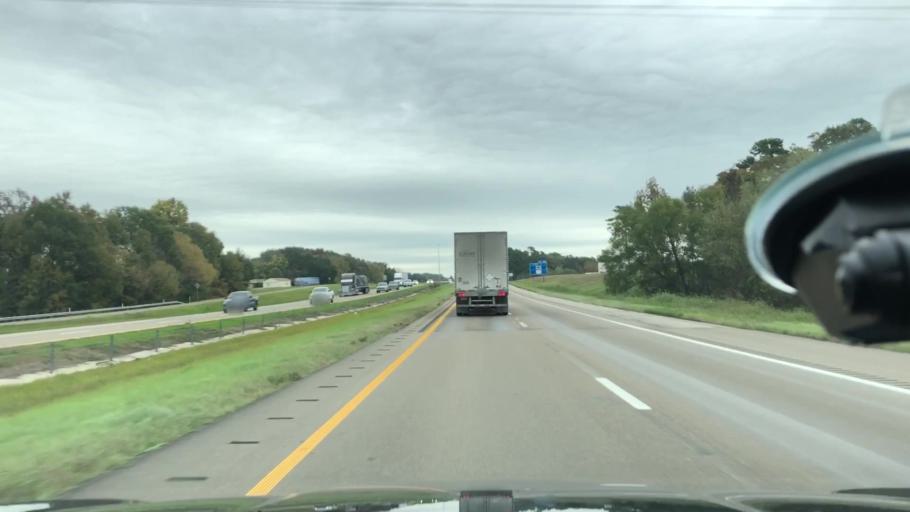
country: US
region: Texas
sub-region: Titus County
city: Mount Pleasant
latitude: 33.1651
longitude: -95.0142
